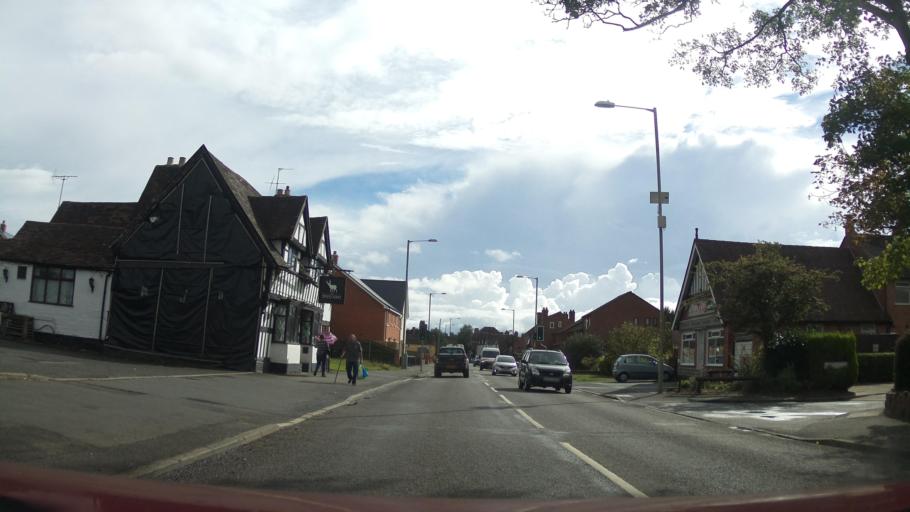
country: GB
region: England
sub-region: Shropshire
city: Shifnal
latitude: 52.6713
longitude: -2.3722
